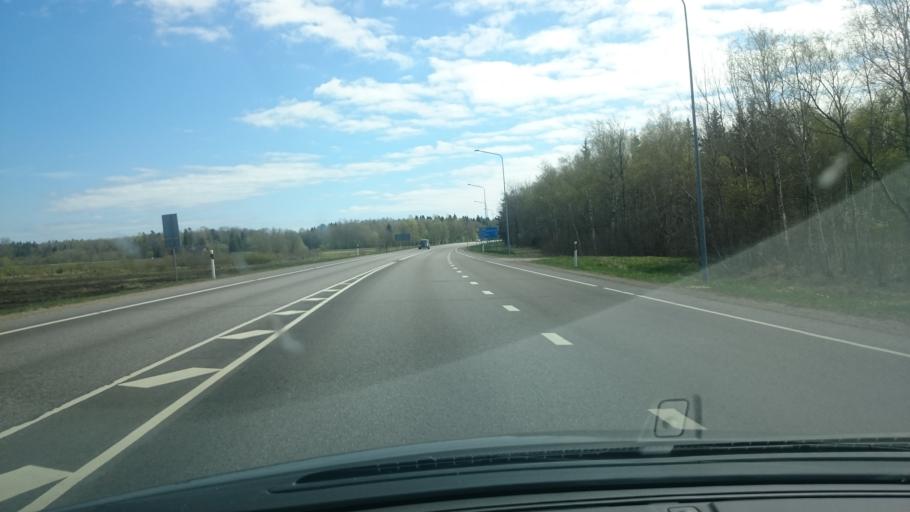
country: EE
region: Ida-Virumaa
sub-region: Kohtla-Jaerve linn
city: Kohtla-Jarve
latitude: 59.4202
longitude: 27.2786
